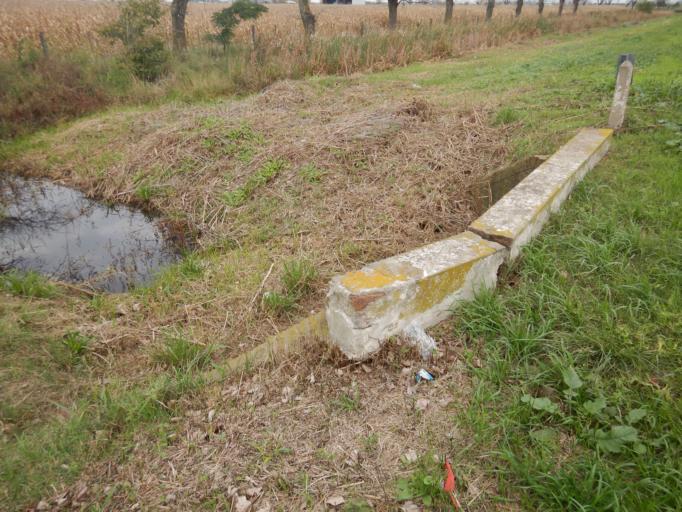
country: AR
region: Santa Fe
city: Roldan
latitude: -32.9017
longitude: -60.9305
